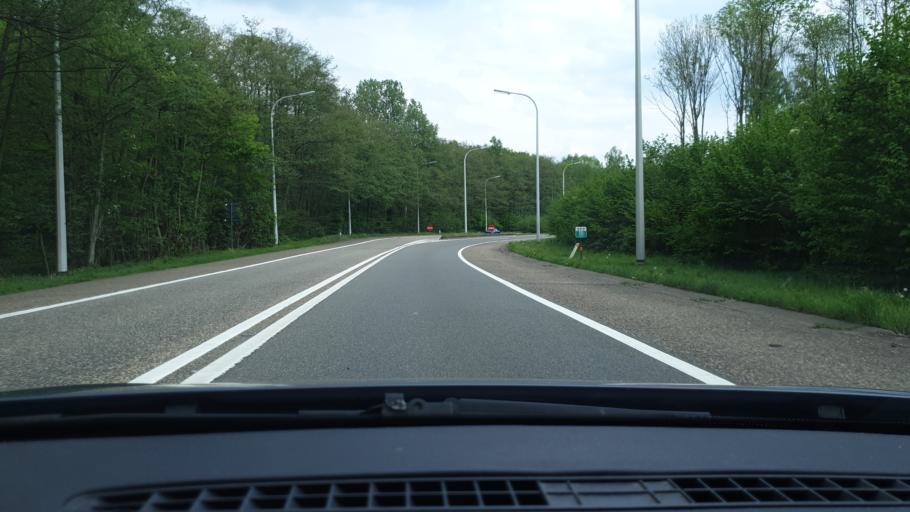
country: BE
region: Flanders
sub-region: Provincie Limburg
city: Houthalen
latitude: 51.0141
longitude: 5.3747
